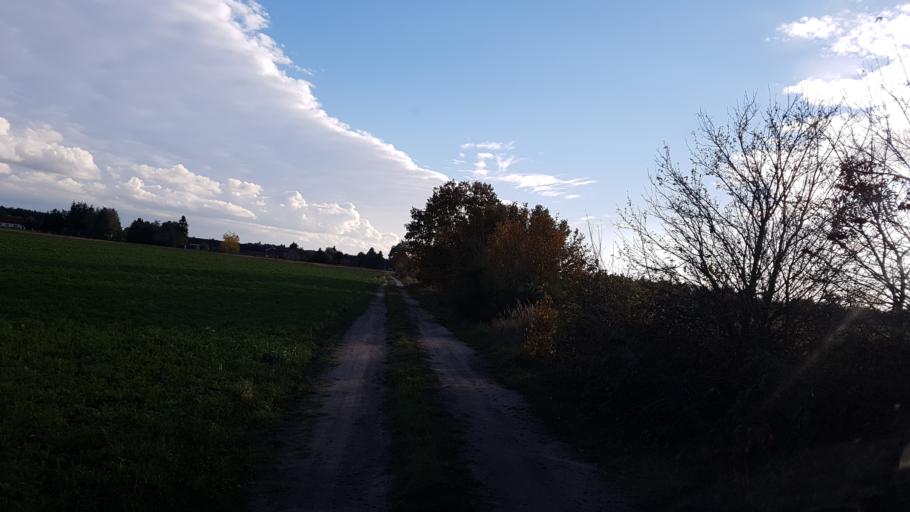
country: DE
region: Brandenburg
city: Finsterwalde
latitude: 51.5739
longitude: 13.6716
